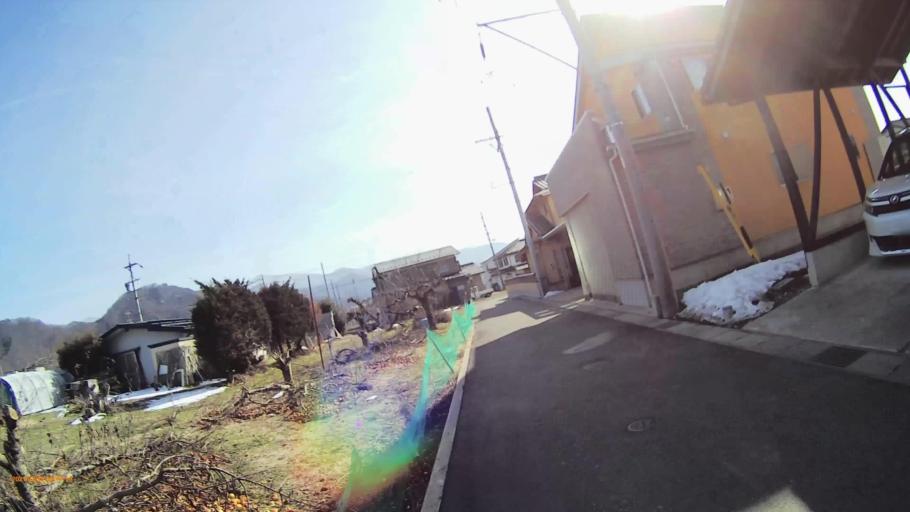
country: JP
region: Nagano
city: Nakano
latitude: 36.7528
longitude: 138.3737
